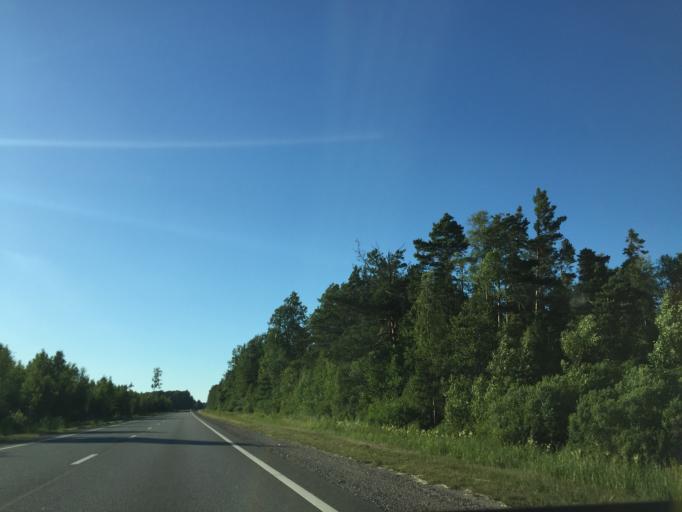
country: LV
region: Ventspils
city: Ventspils
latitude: 57.3810
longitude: 21.7126
